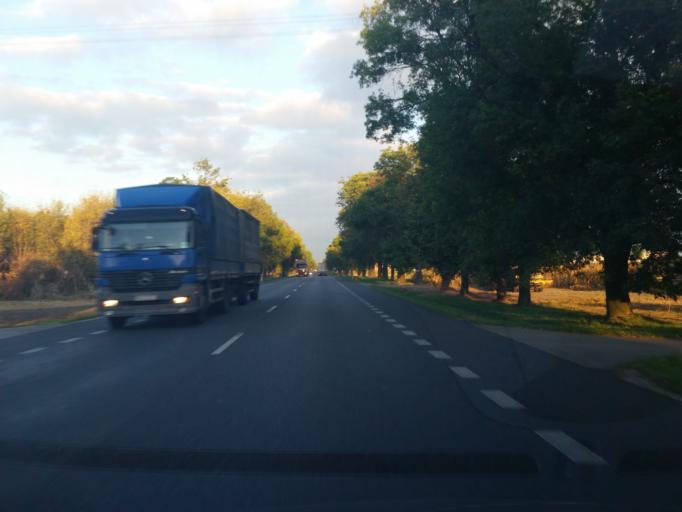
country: PL
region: Masovian Voivodeship
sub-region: Powiat warszawski zachodni
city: Jozefow
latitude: 52.2123
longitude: 20.7193
